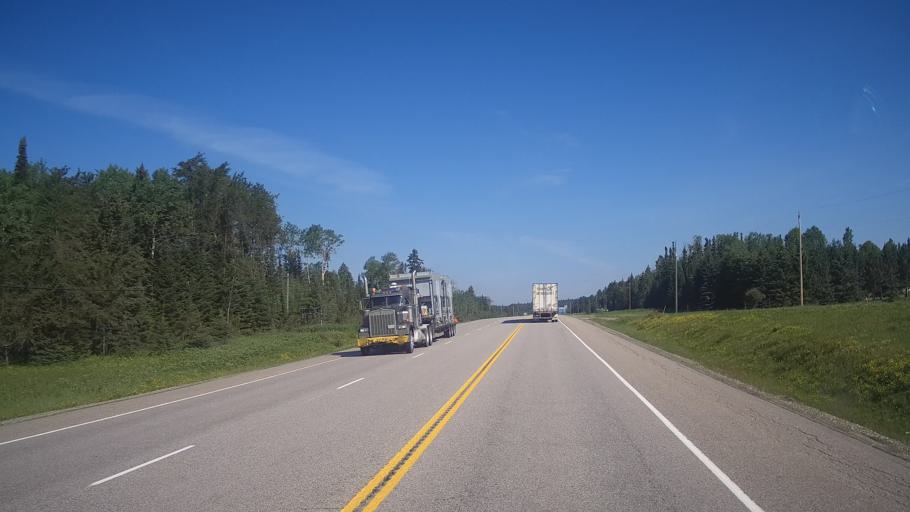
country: CA
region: Ontario
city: Dryden
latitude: 49.7099
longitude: -92.5881
